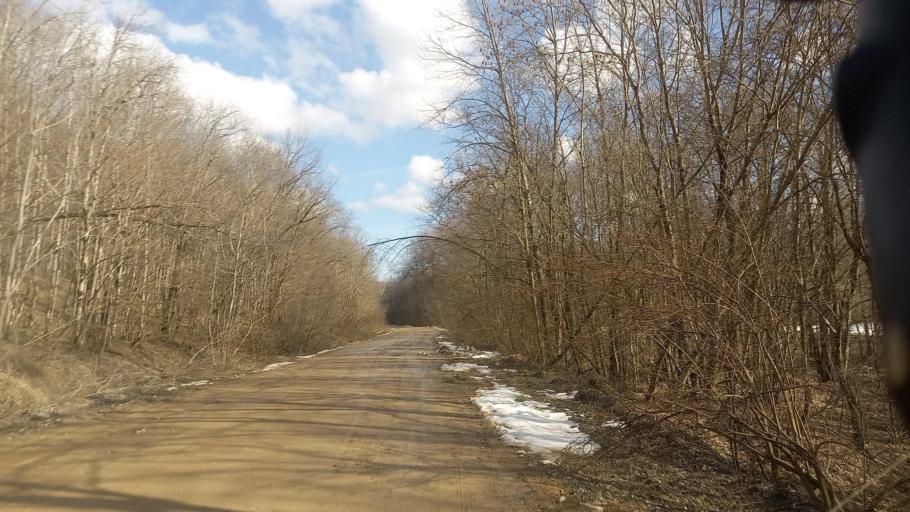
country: RU
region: Krasnodarskiy
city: Smolenskaya
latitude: 44.5979
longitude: 38.8349
